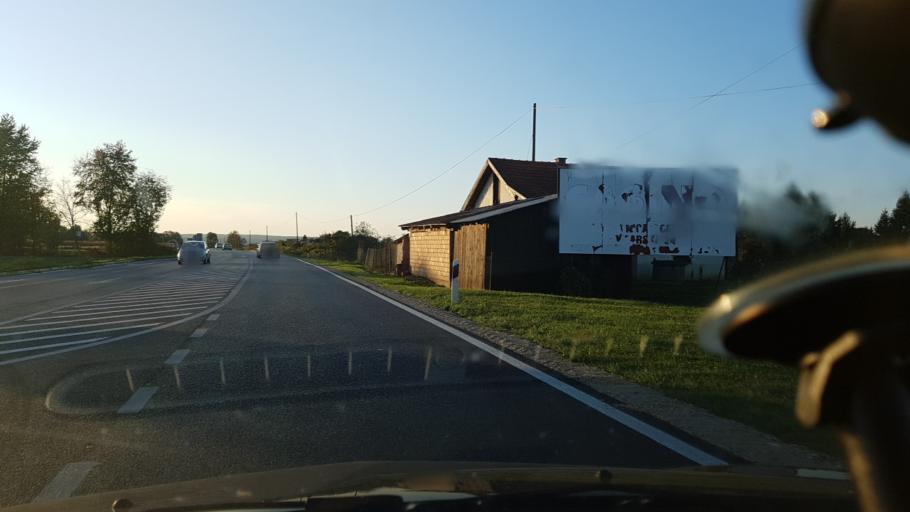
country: HR
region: Koprivnicko-Krizevacka
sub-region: Grad Koprivnica
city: Koprivnica
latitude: 46.1374
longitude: 16.8562
